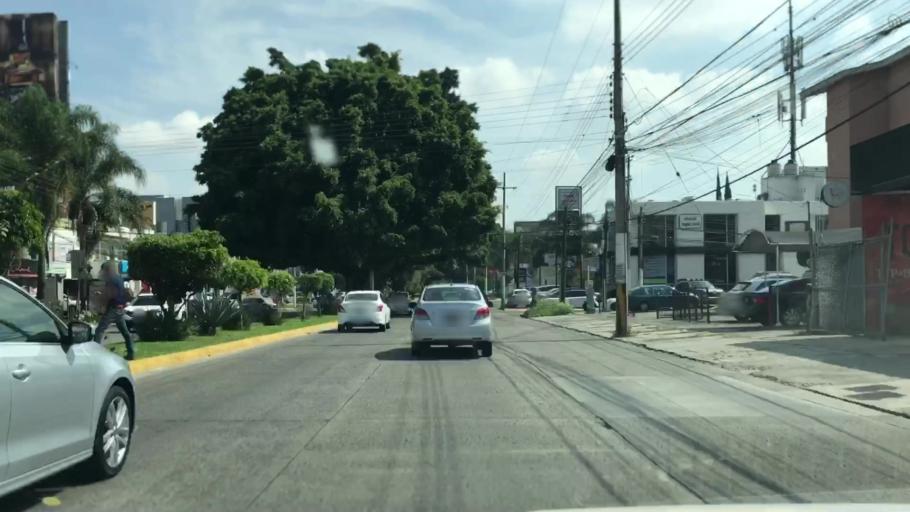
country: MX
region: Jalisco
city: Guadalajara
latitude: 20.6638
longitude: -103.4157
